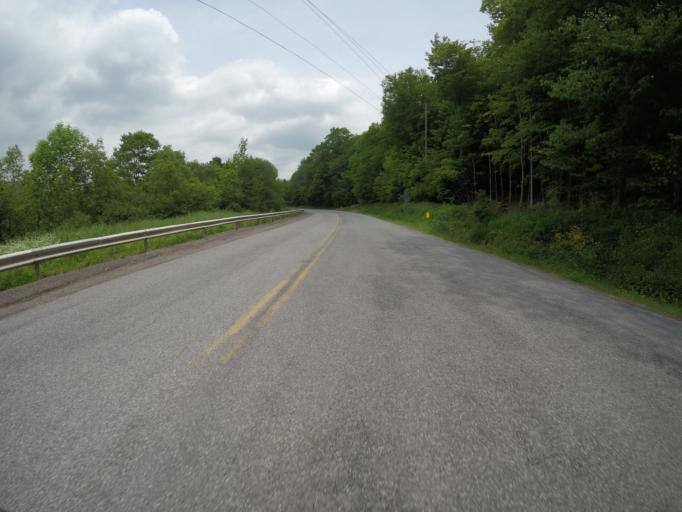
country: US
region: New York
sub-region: Delaware County
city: Stamford
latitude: 42.1831
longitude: -74.6709
